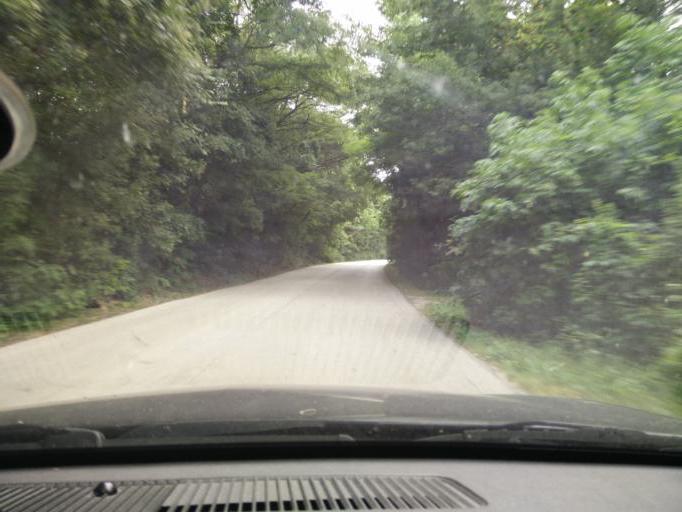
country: HU
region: Komarom-Esztergom
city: Baj
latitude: 47.6654
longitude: 18.3976
